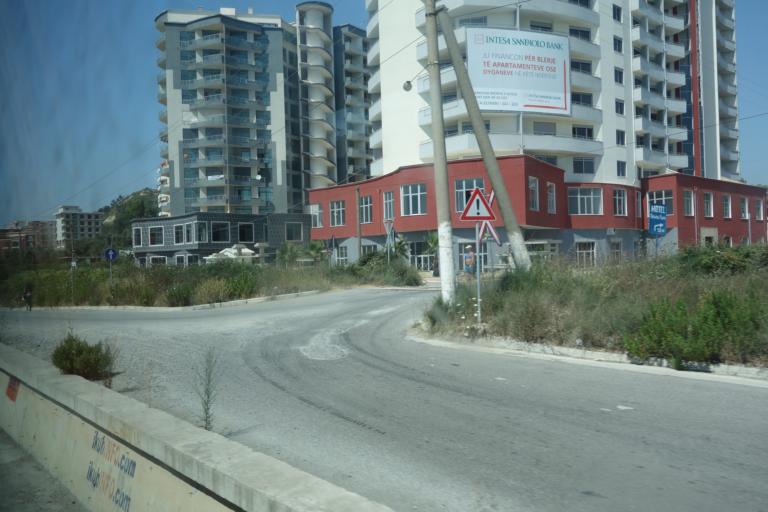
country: AL
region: Tirane
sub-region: Rrethi i Kavajes
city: Golem
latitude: 41.2670
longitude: 19.5222
